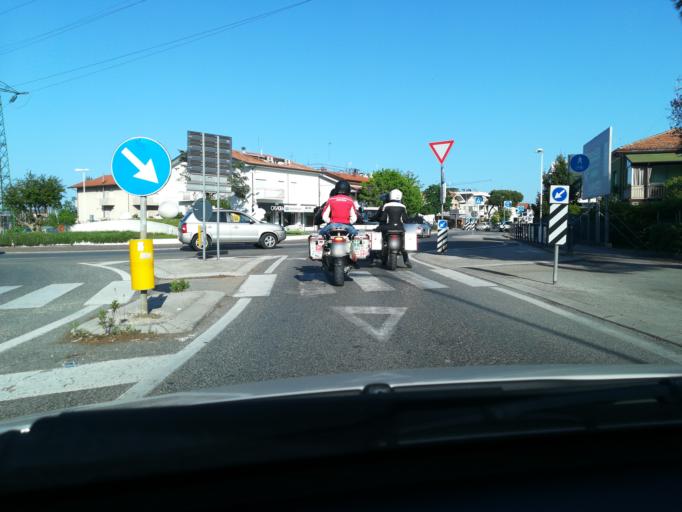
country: IT
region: Emilia-Romagna
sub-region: Provincia di Rimini
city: Riccione
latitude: 43.9927
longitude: 12.6621
